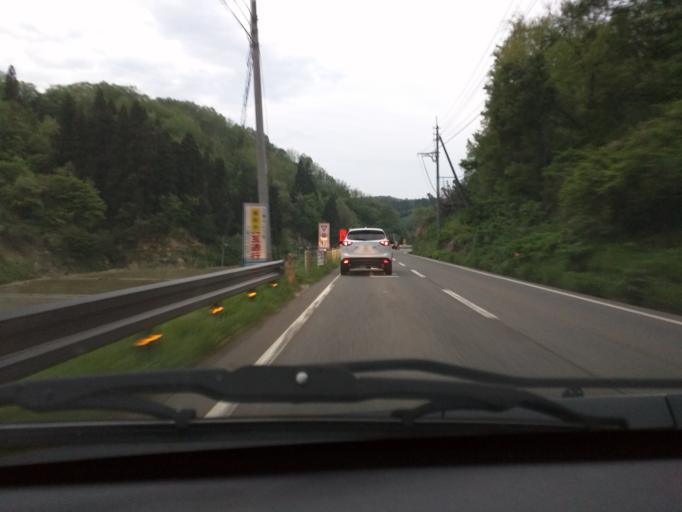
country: JP
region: Niigata
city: Ojiya
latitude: 37.3151
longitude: 138.7367
